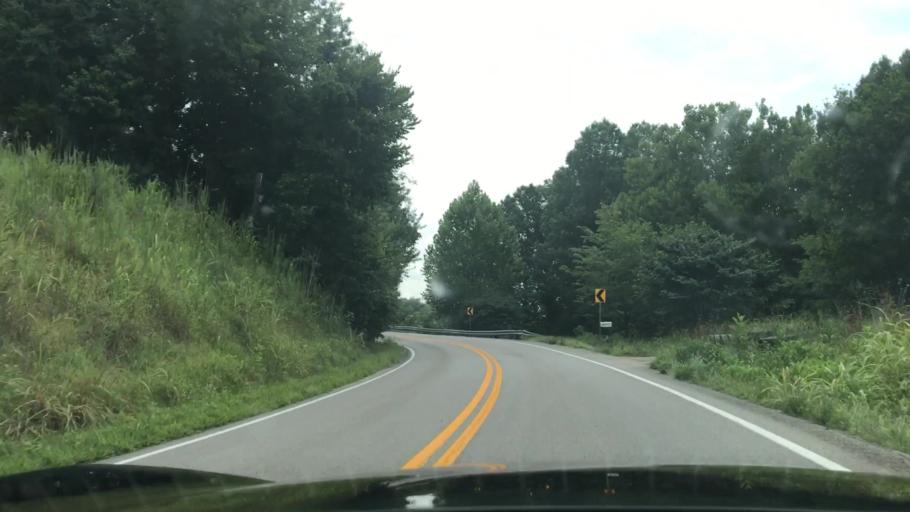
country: US
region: Kentucky
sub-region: Ohio County
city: Beaver Dam
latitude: 37.2125
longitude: -86.9140
